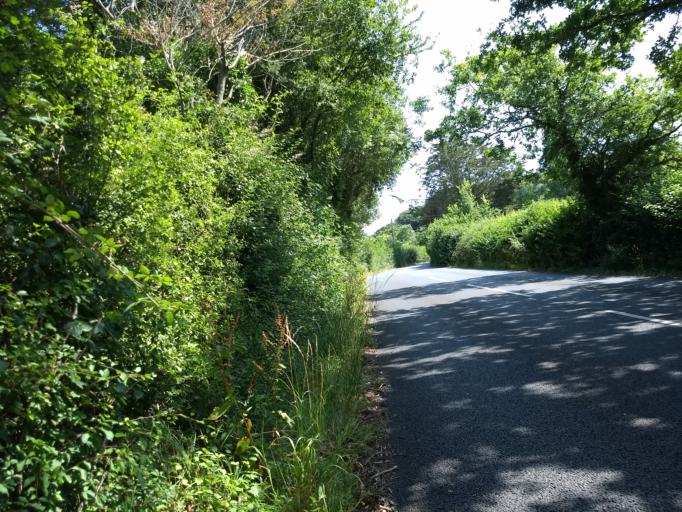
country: GB
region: England
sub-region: Isle of Wight
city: Northwood
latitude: 50.7298
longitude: -1.3299
